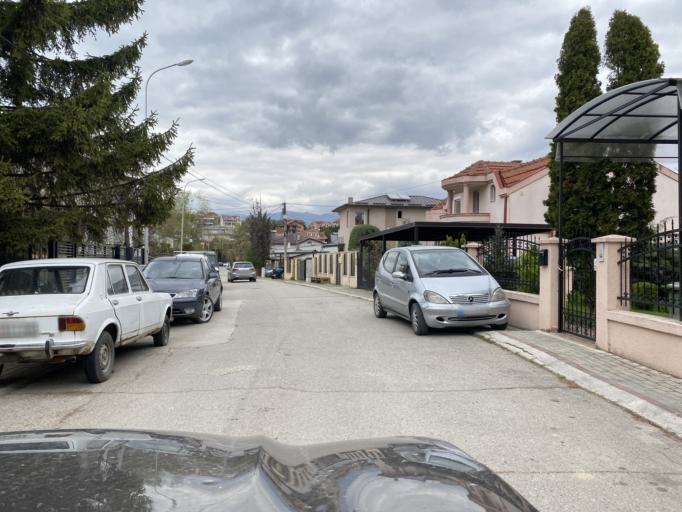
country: MK
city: Radishani
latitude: 42.0641
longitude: 21.4495
